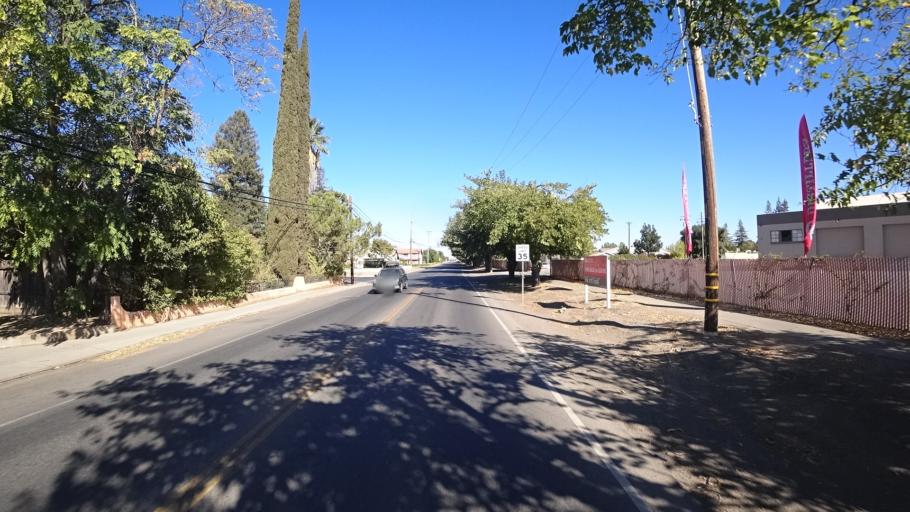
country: US
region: California
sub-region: Yolo County
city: Winters
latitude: 38.5268
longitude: -121.9710
